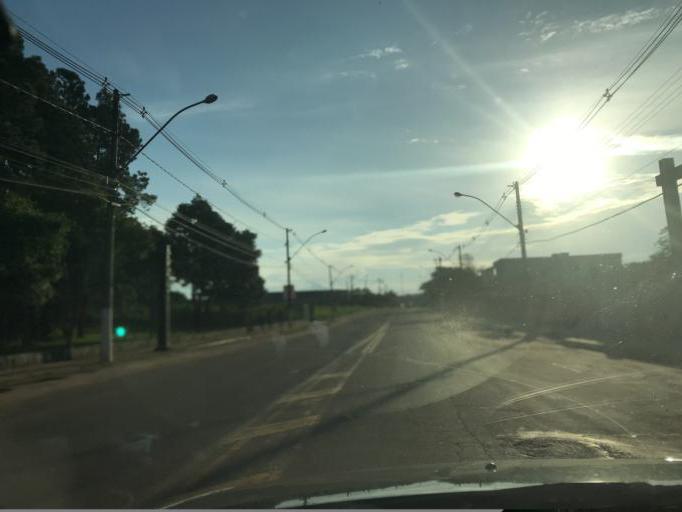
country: BR
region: Minas Gerais
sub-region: Tres Coracoes
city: Tres Coracoes
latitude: -21.7017
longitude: -45.2412
